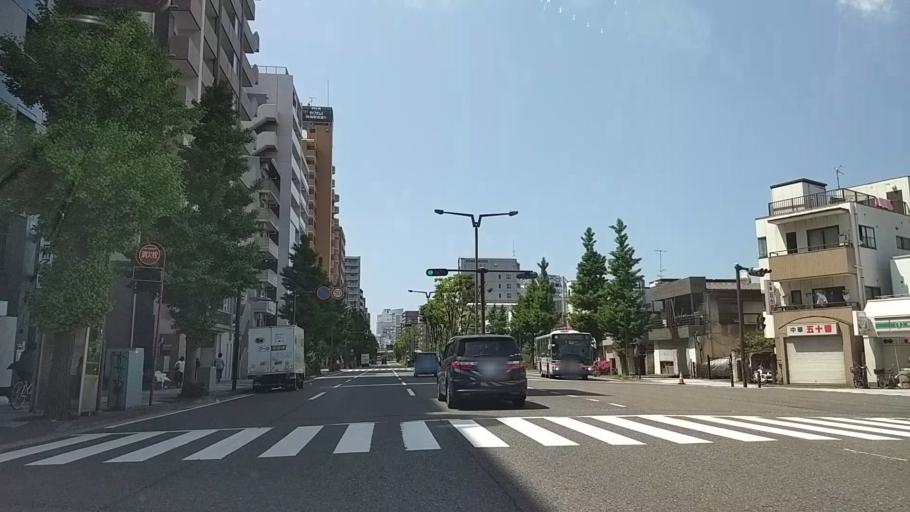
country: JP
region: Kanagawa
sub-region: Kawasaki-shi
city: Kawasaki
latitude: 35.5225
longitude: 139.7111
